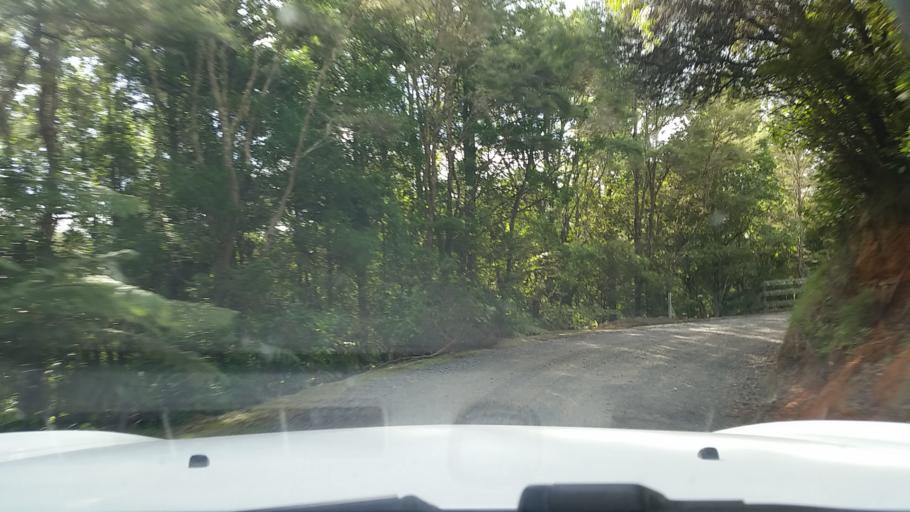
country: NZ
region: Waikato
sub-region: Hauraki District
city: Ngatea
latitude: -37.4661
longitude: 175.4566
